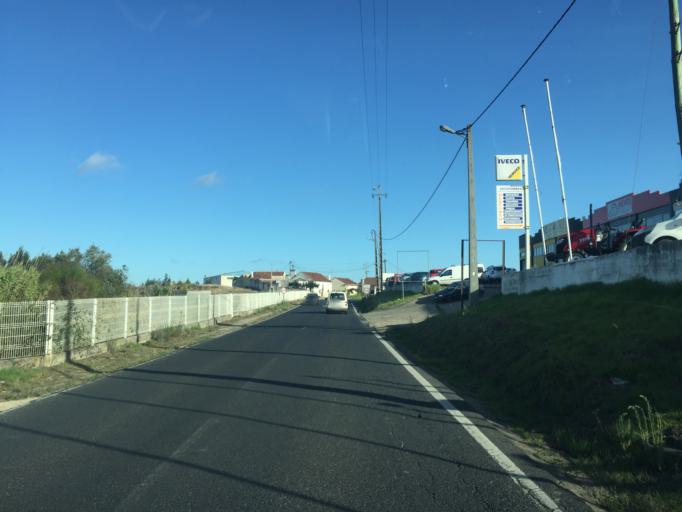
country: PT
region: Lisbon
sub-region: Torres Vedras
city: Torres Vedras
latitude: 39.1124
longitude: -9.2626
